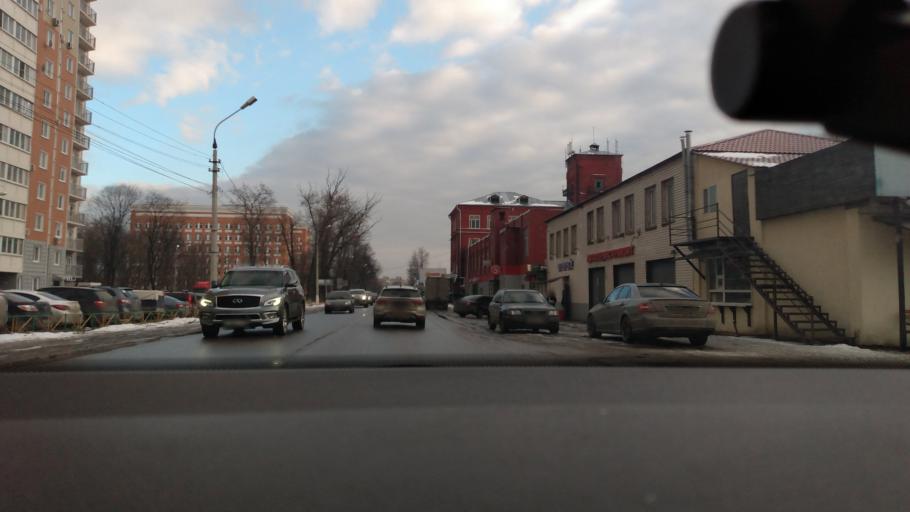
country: RU
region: Moskovskaya
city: Zheleznodorozhnyy
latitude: 55.7291
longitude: 38.0299
